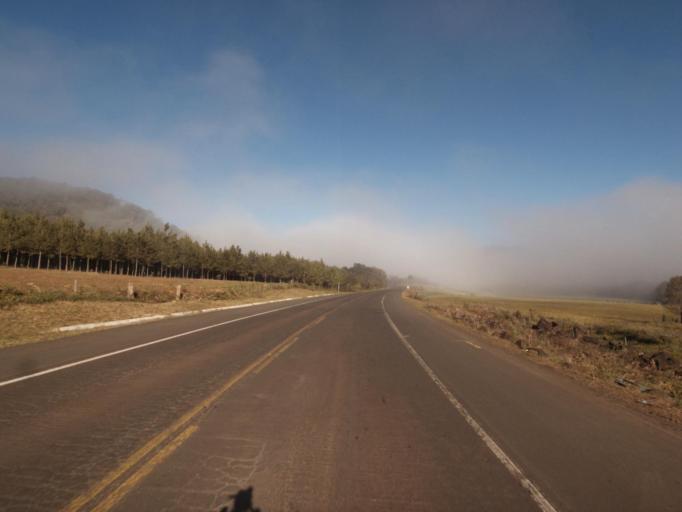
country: BR
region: Rio Grande do Sul
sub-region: Frederico Westphalen
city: Frederico Westphalen
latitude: -26.9788
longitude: -53.2159
